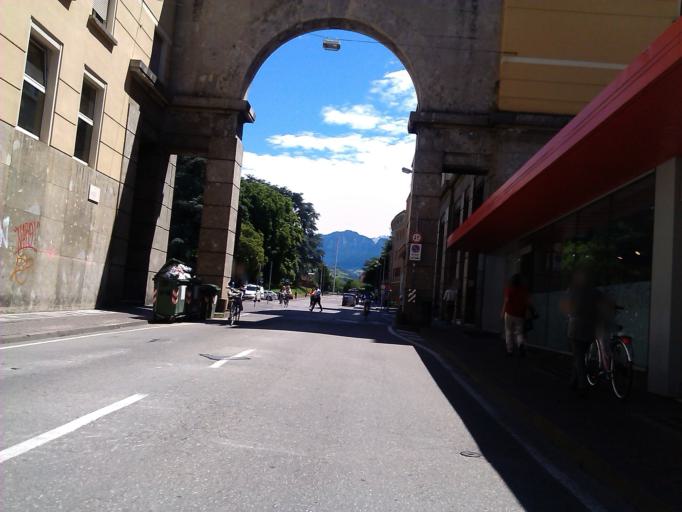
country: IT
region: Trentino-Alto Adige
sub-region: Bolzano
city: Bolzano
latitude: 46.5003
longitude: 11.3425
